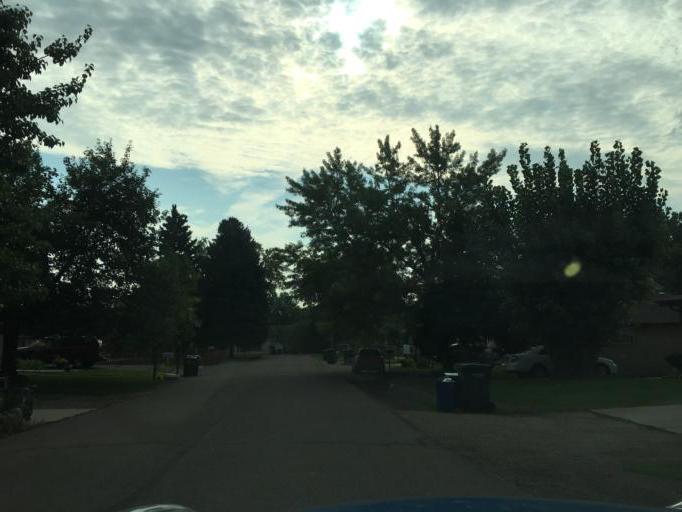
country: US
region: Colorado
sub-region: Jefferson County
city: Wheat Ridge
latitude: 39.7449
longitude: -105.1078
